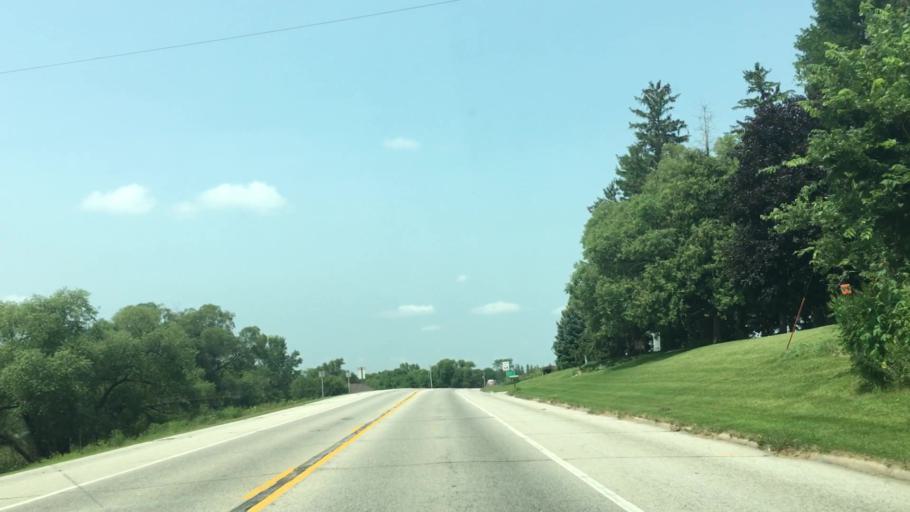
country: US
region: Iowa
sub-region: Fayette County
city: Oelwein
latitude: 42.6242
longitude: -91.9080
